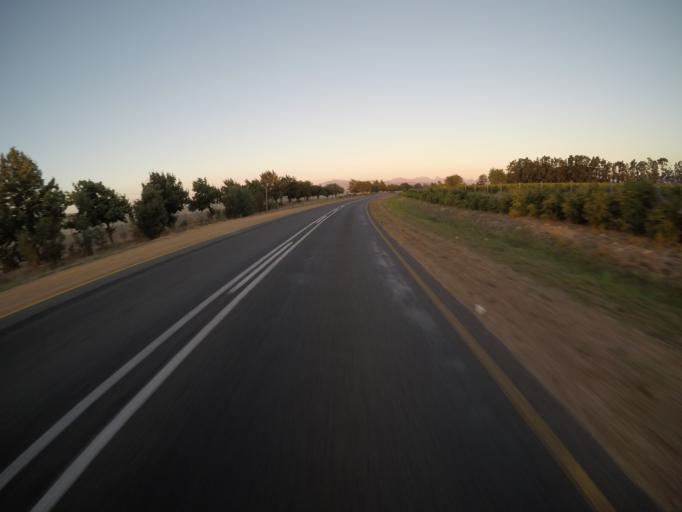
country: ZA
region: Western Cape
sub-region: Cape Winelands District Municipality
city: Paarl
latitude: -33.8032
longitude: 18.8892
